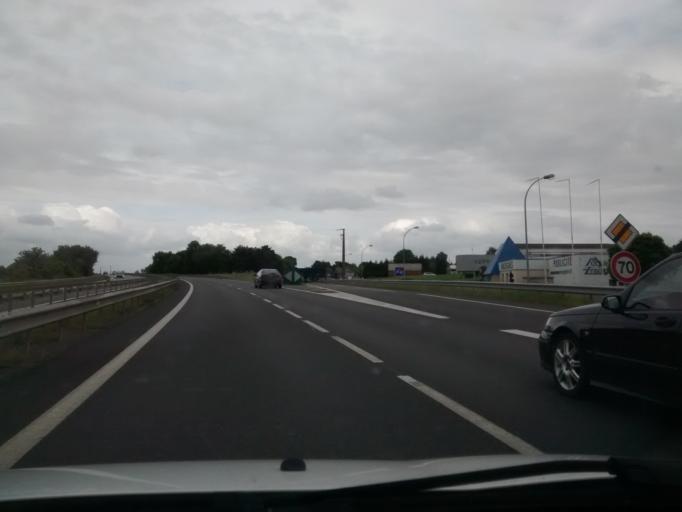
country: FR
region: Brittany
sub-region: Departement d'Ille-et-Vilaine
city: Breal-sous-Montfort
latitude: 48.0597
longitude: -1.8791
